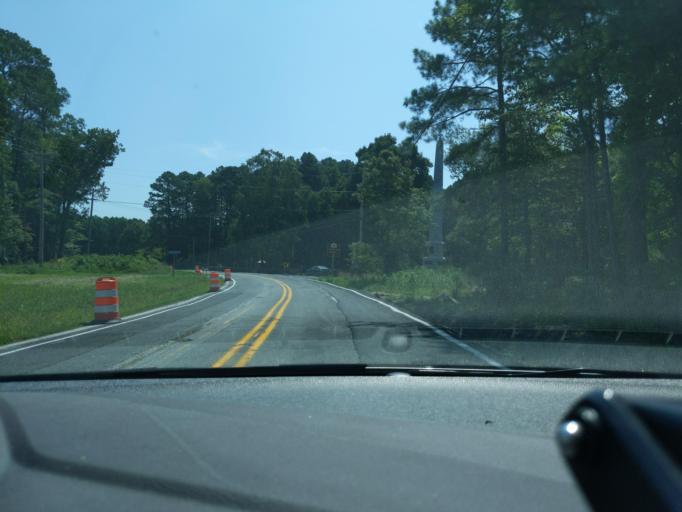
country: US
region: Virginia
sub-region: Northumberland County
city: Heathsville
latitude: 38.0740
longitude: -76.3432
